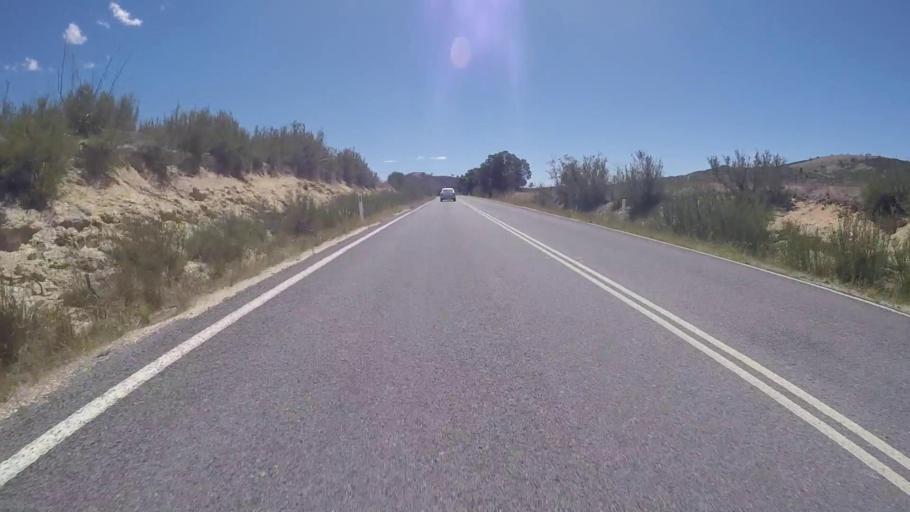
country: AU
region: Australian Capital Territory
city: Macarthur
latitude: -35.4552
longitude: 149.0083
